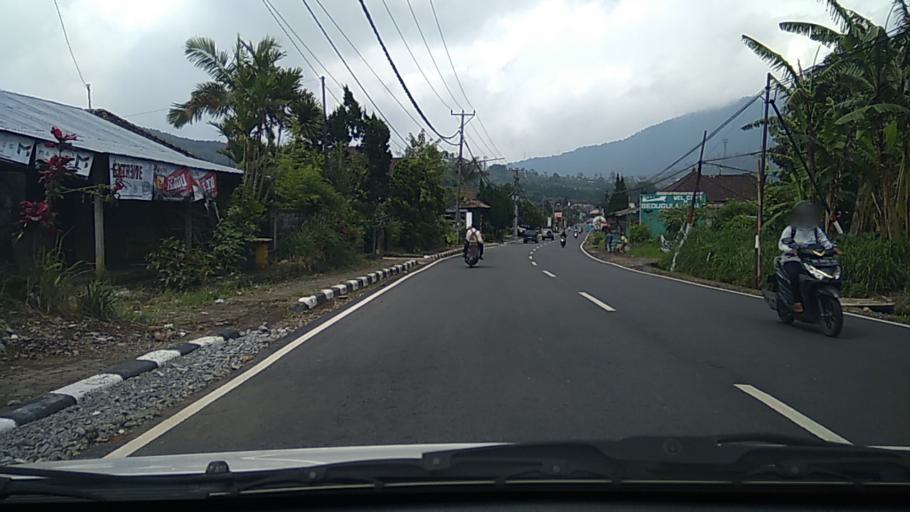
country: ID
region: Bali
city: Munduk
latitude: -8.2741
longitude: 115.1639
